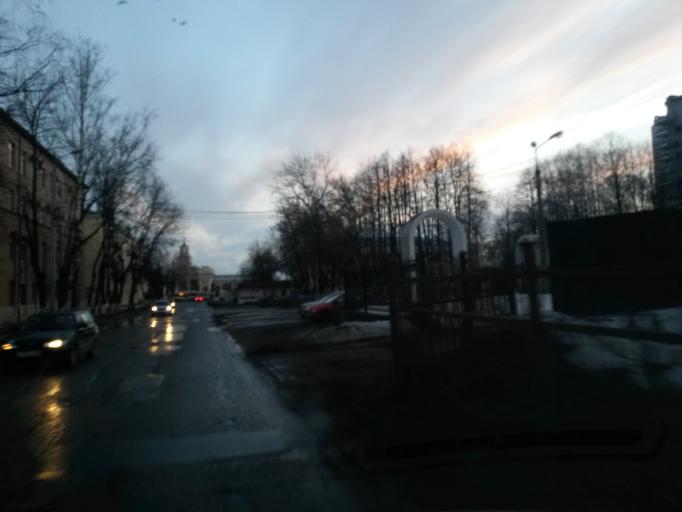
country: RU
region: Jaroslavl
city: Yaroslavl
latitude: 57.6282
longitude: 39.8384
